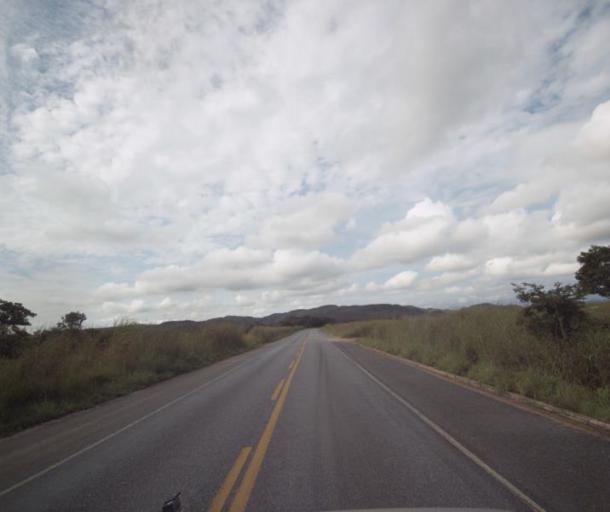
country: BR
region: Goias
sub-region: Pirenopolis
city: Pirenopolis
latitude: -15.5651
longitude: -48.6219
